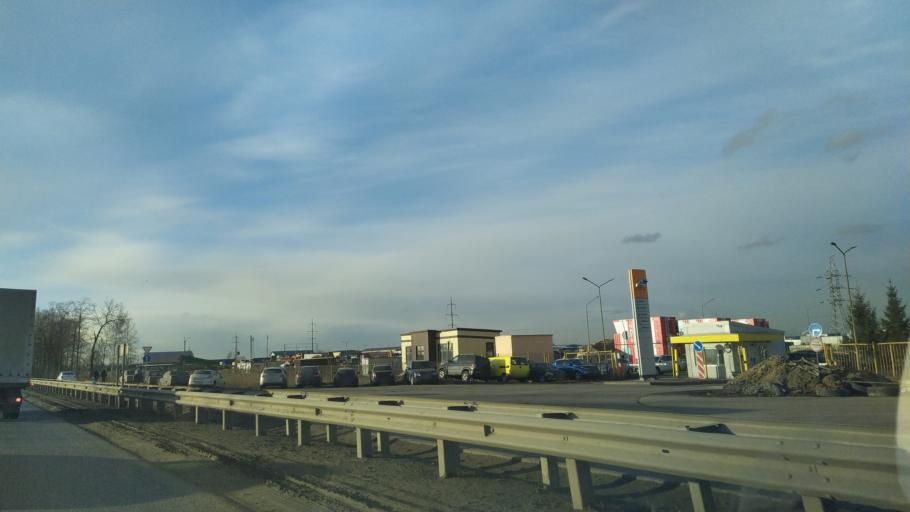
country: RU
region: St.-Petersburg
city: Shushary
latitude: 59.7807
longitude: 30.4374
